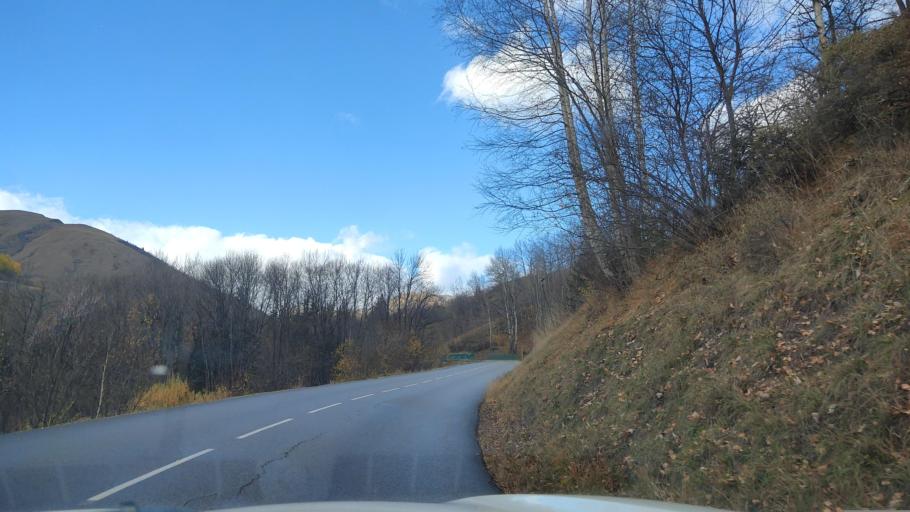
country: FR
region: Rhone-Alpes
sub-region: Departement de la Savoie
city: Saint-Jean-de-Maurienne
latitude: 45.1982
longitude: 6.2786
